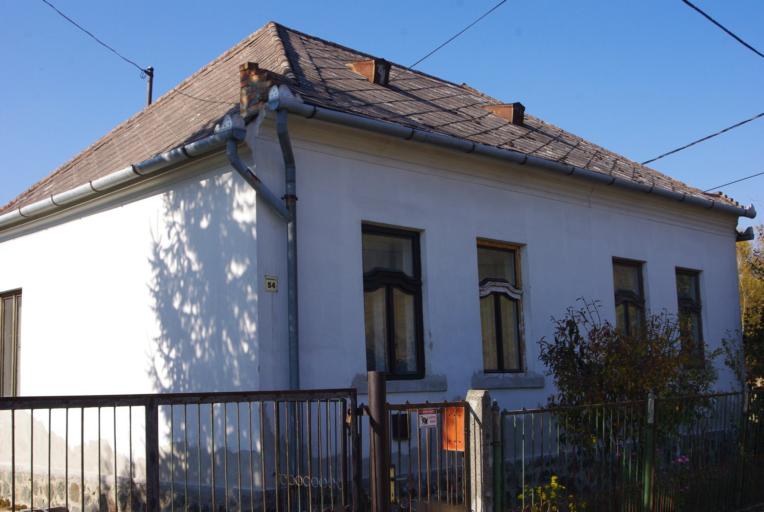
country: HU
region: Borsod-Abauj-Zemplen
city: Borsodnadasd
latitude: 48.0495
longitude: 20.2705
